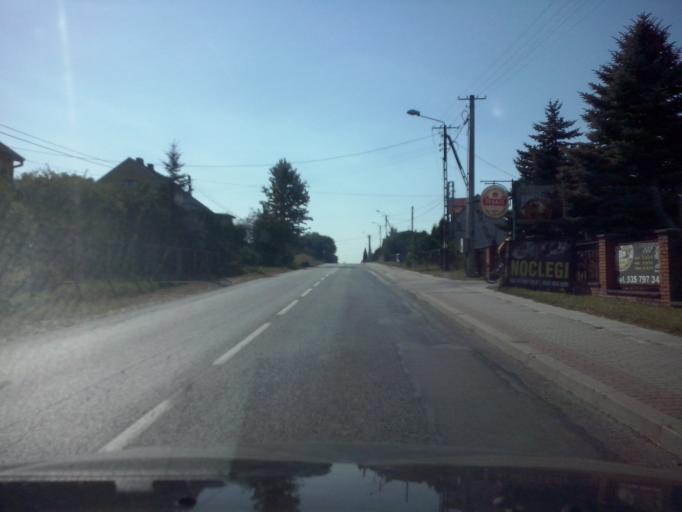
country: PL
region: Swietokrzyskie
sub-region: Powiat kielecki
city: Domaszowice
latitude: 50.8141
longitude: 20.6929
